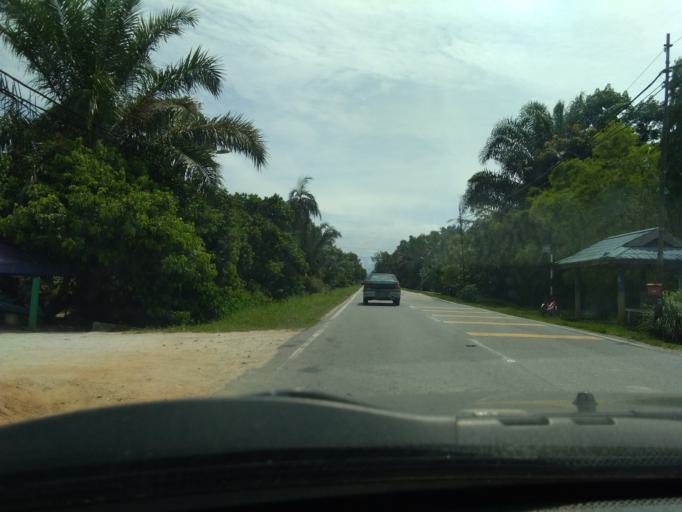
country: MY
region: Perak
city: Bagan Serai
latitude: 5.0446
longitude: 100.5788
